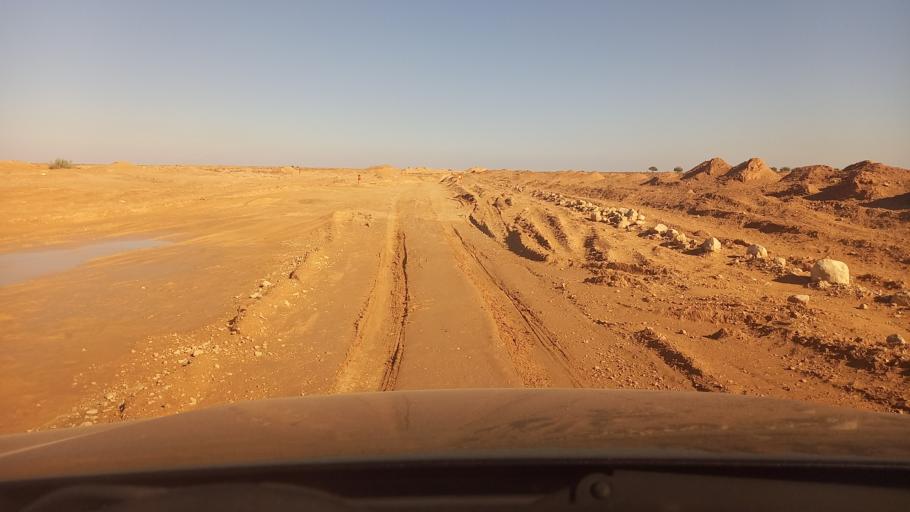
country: TN
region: Madanin
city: Medenine
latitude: 33.1464
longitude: 10.5067
